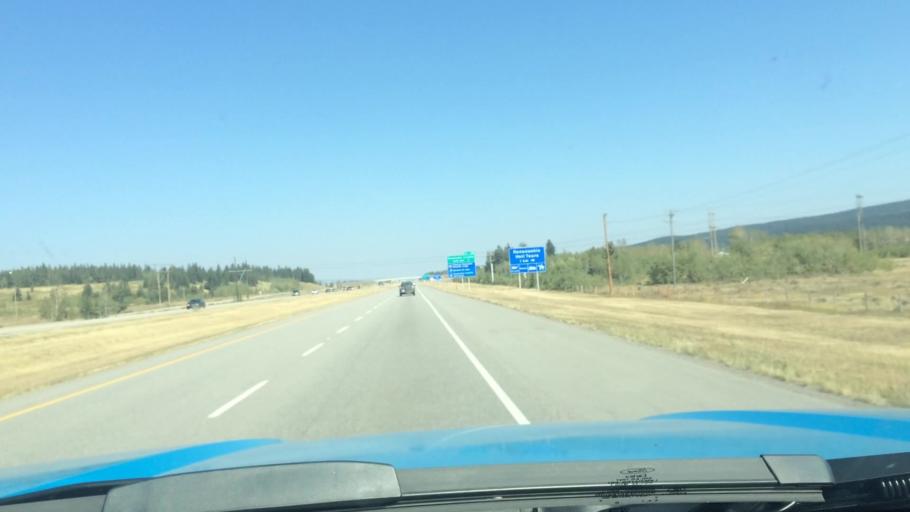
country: CA
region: Alberta
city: Canmore
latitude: 51.0975
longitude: -115.0362
